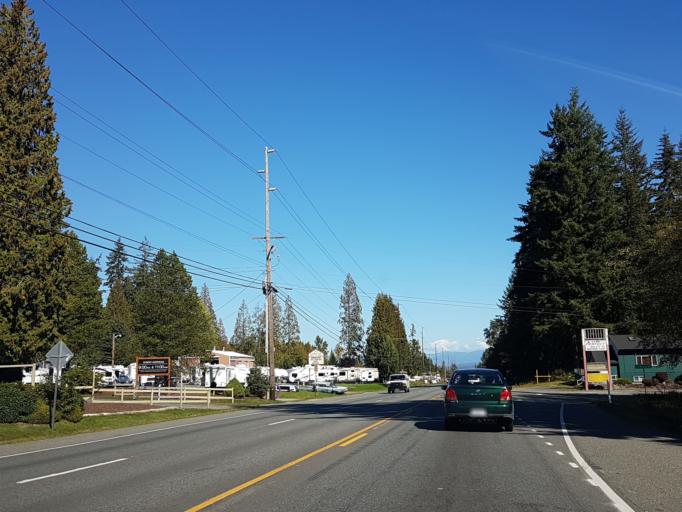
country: US
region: Washington
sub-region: Snohomish County
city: Clearview
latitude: 47.8407
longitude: -122.1221
